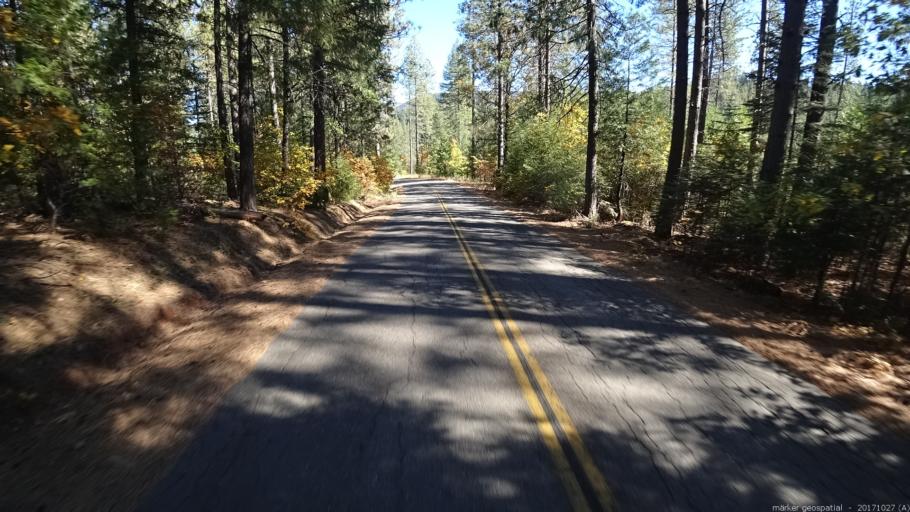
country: US
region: California
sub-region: Shasta County
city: Shingletown
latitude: 40.7314
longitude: -121.9247
